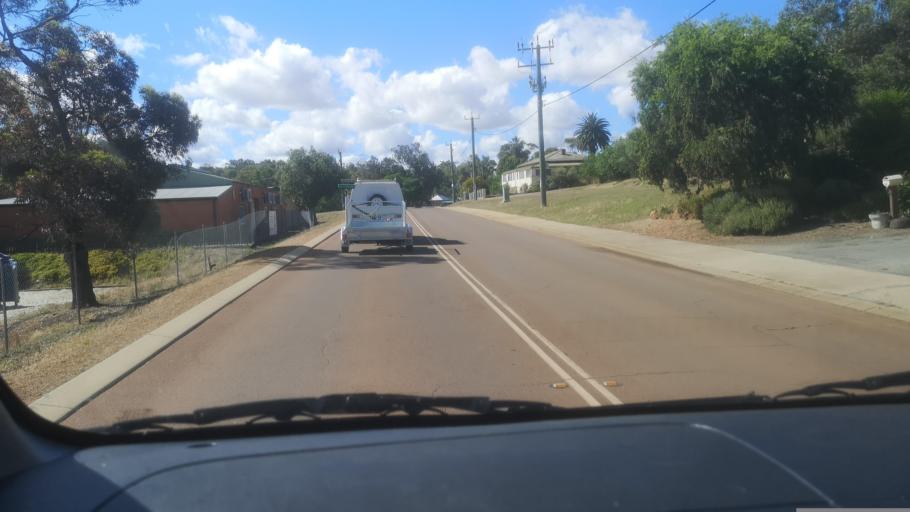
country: AU
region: Western Australia
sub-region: Toodyay
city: Toodyay
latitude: -31.5470
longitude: 116.4609
